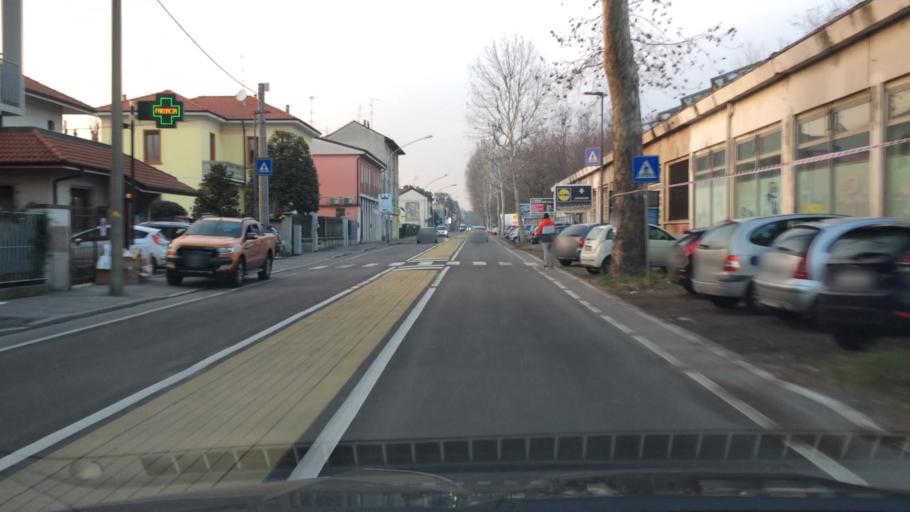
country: IT
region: Lombardy
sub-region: Provincia di Varese
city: Saronno
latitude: 45.6184
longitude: 9.0307
